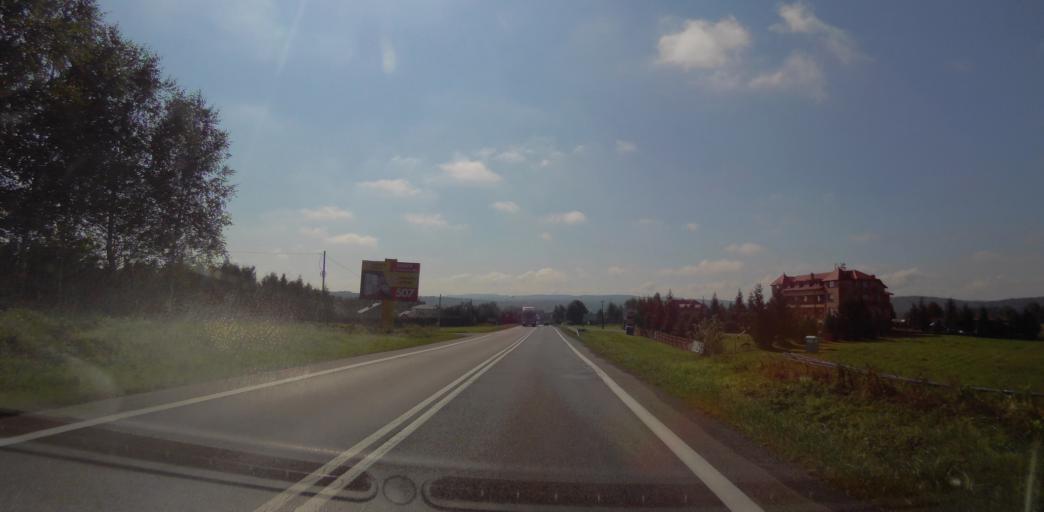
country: PL
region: Subcarpathian Voivodeship
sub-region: Powiat sanocki
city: Strachocina
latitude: 49.5801
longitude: 22.1452
